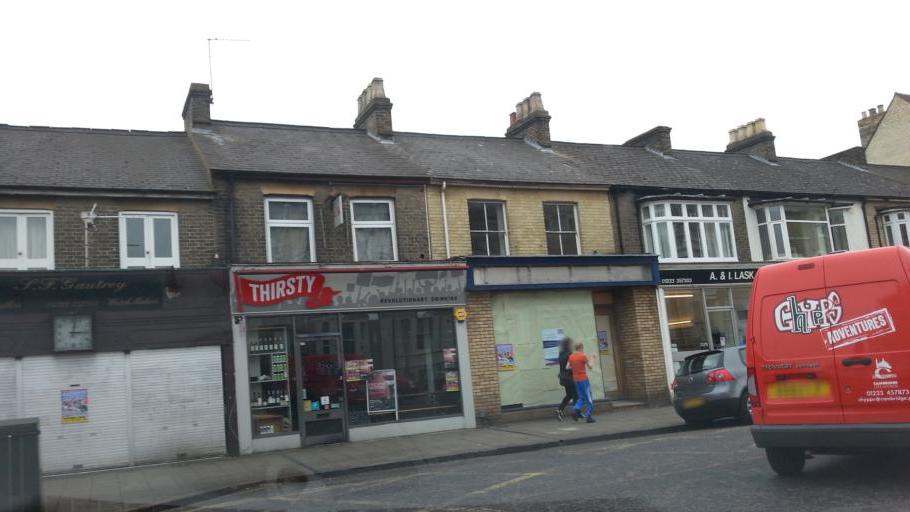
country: GB
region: England
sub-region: Cambridgeshire
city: Cambridge
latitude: 52.2146
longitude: 0.1265
